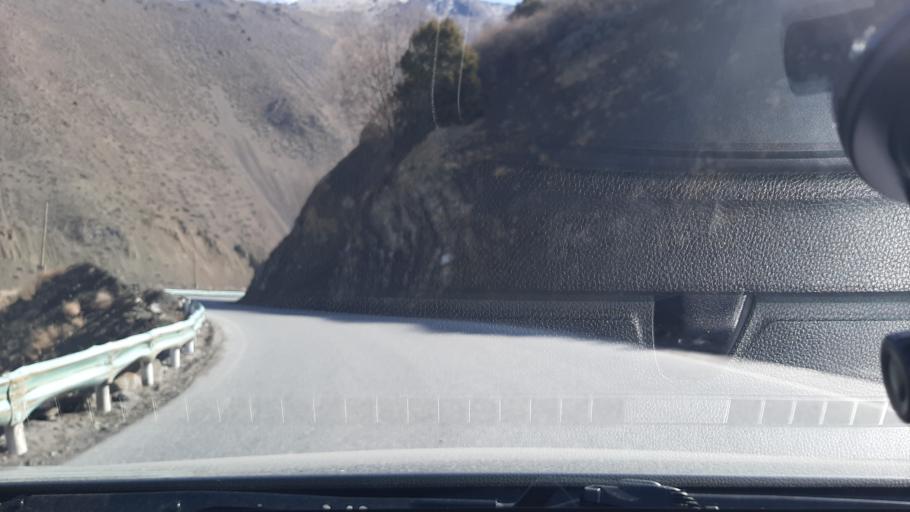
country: TJ
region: Viloyati Sughd
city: Ayni
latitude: 39.4576
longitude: 68.5541
